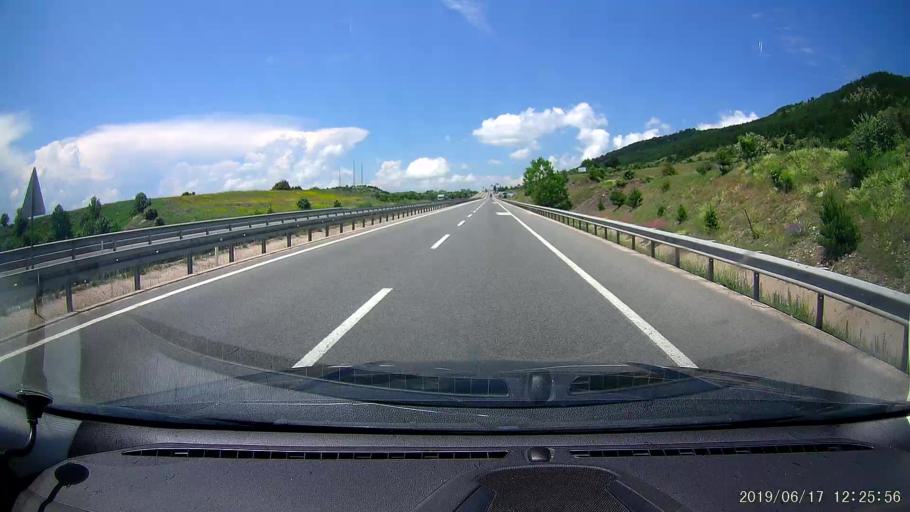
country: TR
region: Bolu
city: Gerede
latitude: 40.8208
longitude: 32.3119
